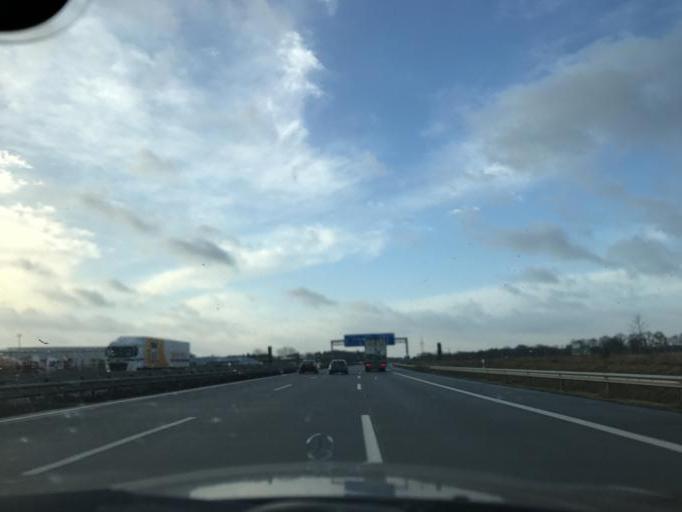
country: DE
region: Lower Saxony
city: Reessum
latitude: 53.1175
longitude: 9.2083
